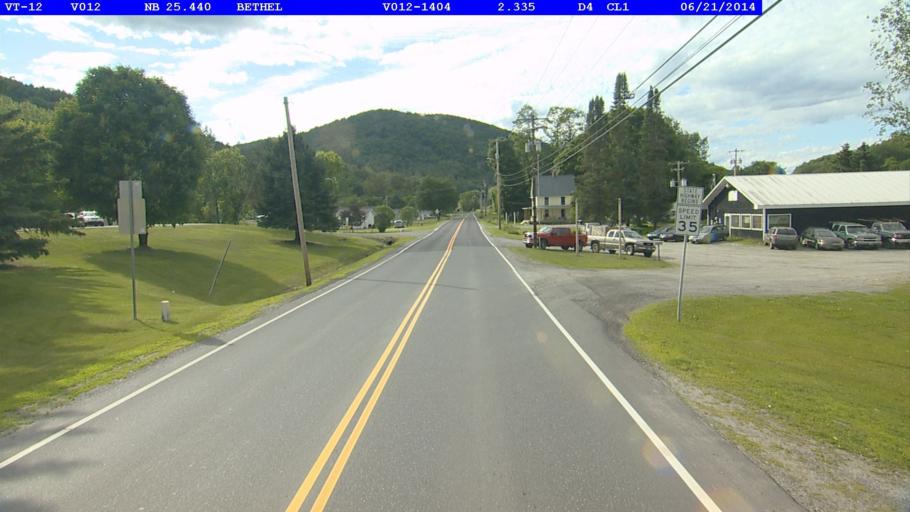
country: US
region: Vermont
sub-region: Orange County
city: Randolph
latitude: 43.8337
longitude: -72.6425
